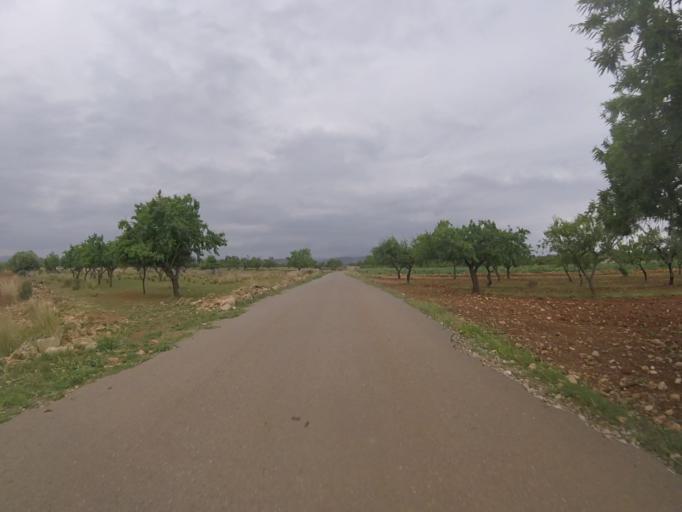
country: ES
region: Valencia
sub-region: Provincia de Castello
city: Torreblanca
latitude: 40.2149
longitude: 0.2362
